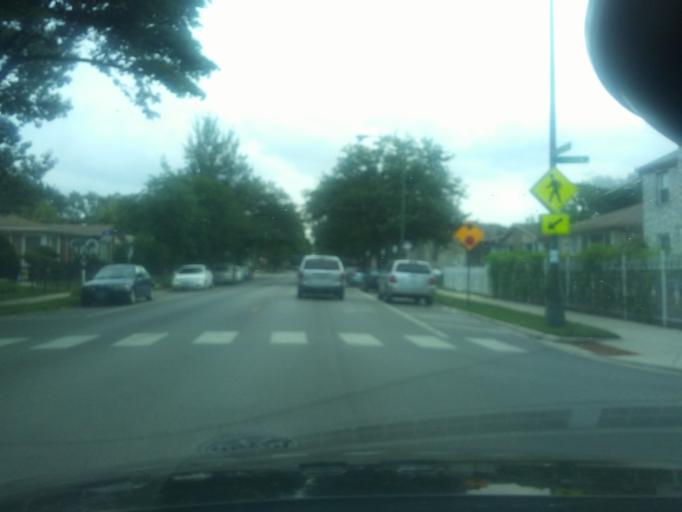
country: US
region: Illinois
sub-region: Cook County
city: Evanston
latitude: 42.0166
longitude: -87.6997
